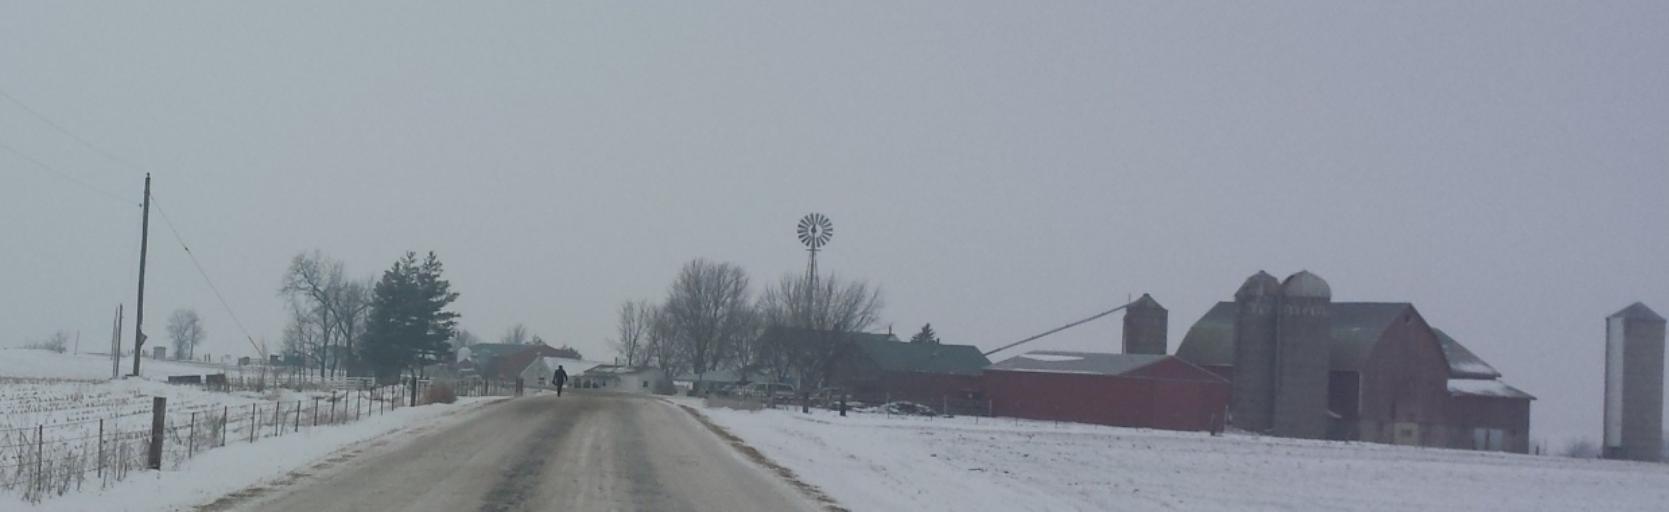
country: US
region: Wisconsin
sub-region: Monroe County
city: Cashton
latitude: 43.7690
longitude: -90.6569
